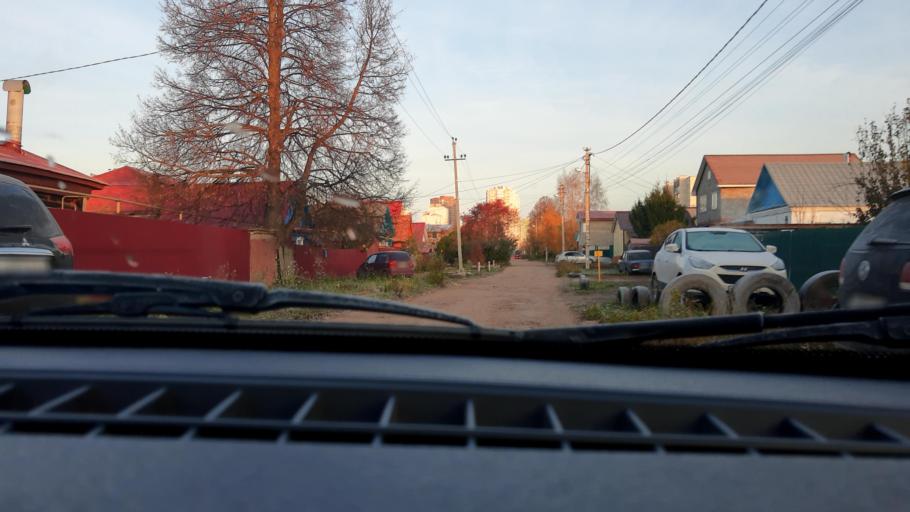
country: RU
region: Bashkortostan
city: Mikhaylovka
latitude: 54.7847
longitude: 55.8795
